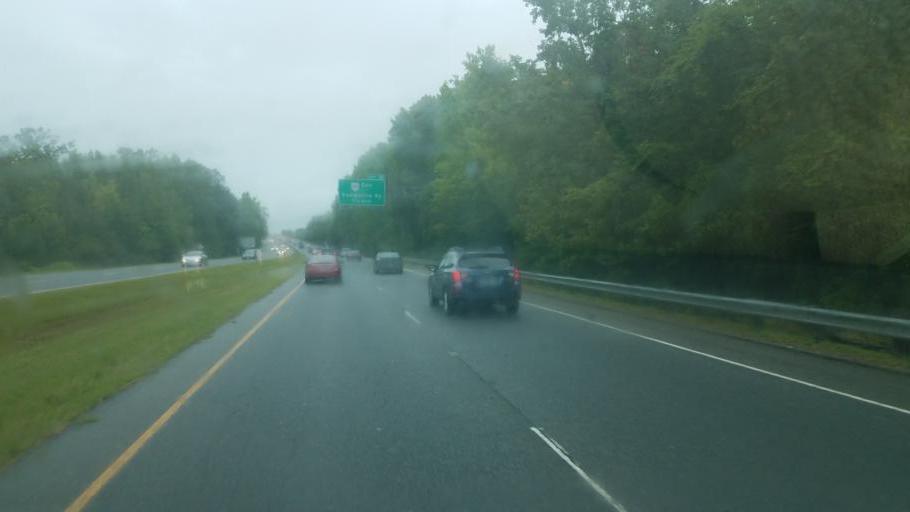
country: US
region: Virginia
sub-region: City of Chesapeake
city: Chesapeake
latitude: 36.7129
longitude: -76.2254
